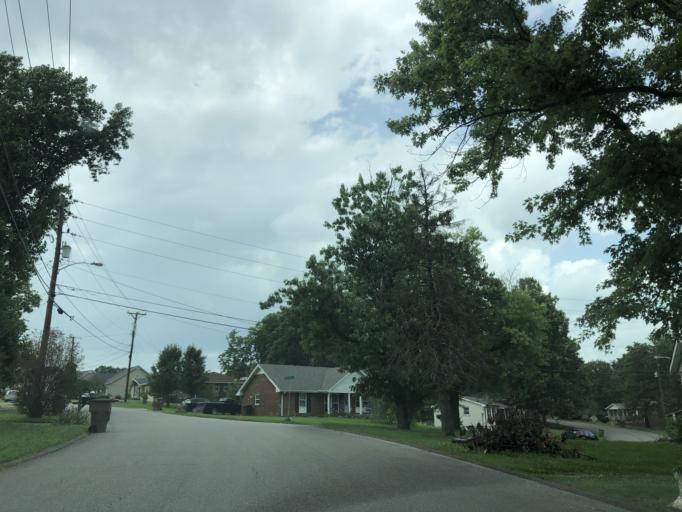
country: US
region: Tennessee
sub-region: Williamson County
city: Brentwood Estates
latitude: 36.0547
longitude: -86.6908
